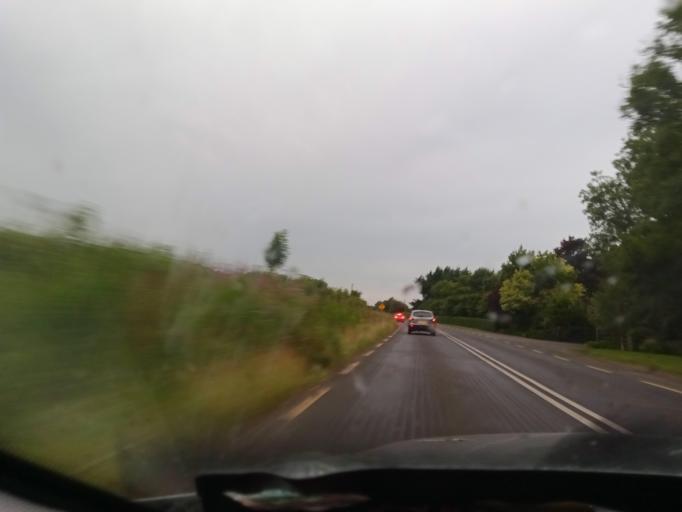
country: IE
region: Leinster
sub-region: Laois
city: Mountmellick
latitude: 53.1232
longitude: -7.3734
